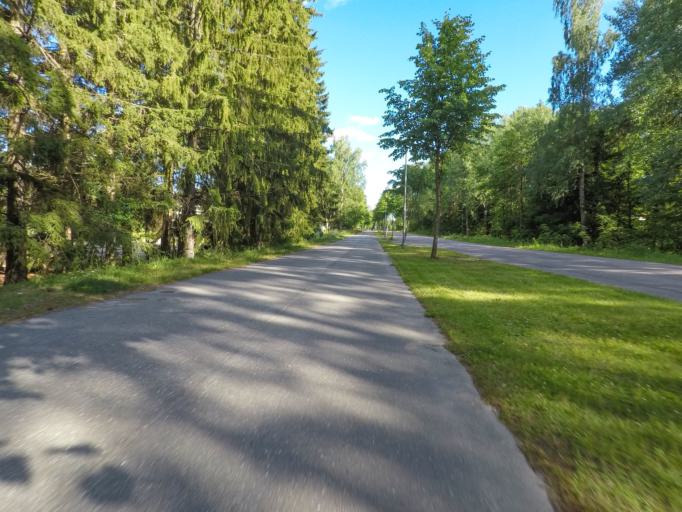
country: FI
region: South Karelia
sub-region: Lappeenranta
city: Lappeenranta
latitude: 61.0712
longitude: 28.1530
